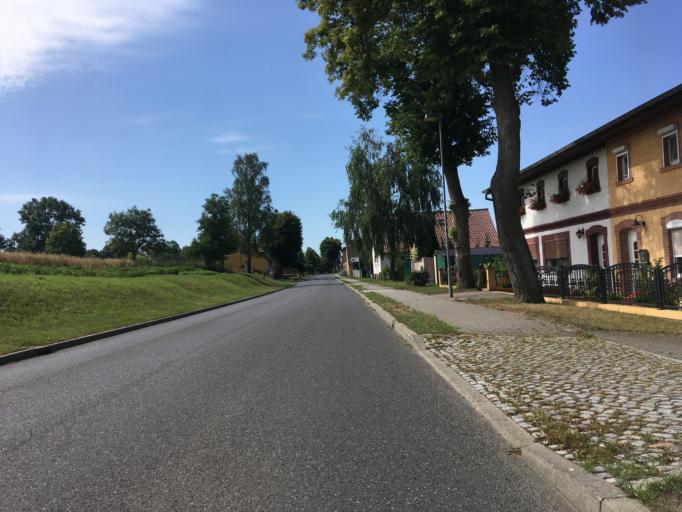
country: DE
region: Brandenburg
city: Zichow
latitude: 53.1908
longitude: 14.0386
